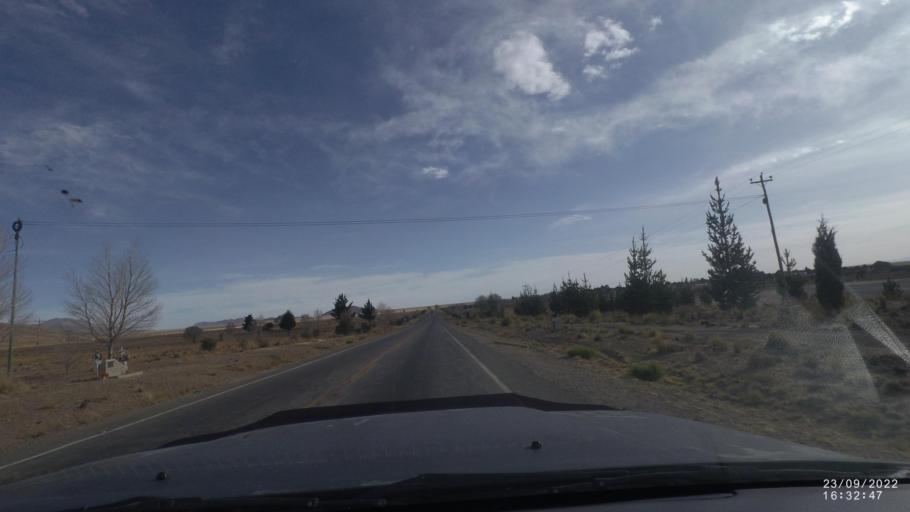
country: BO
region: Oruro
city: Machacamarca
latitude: -18.1659
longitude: -67.0098
